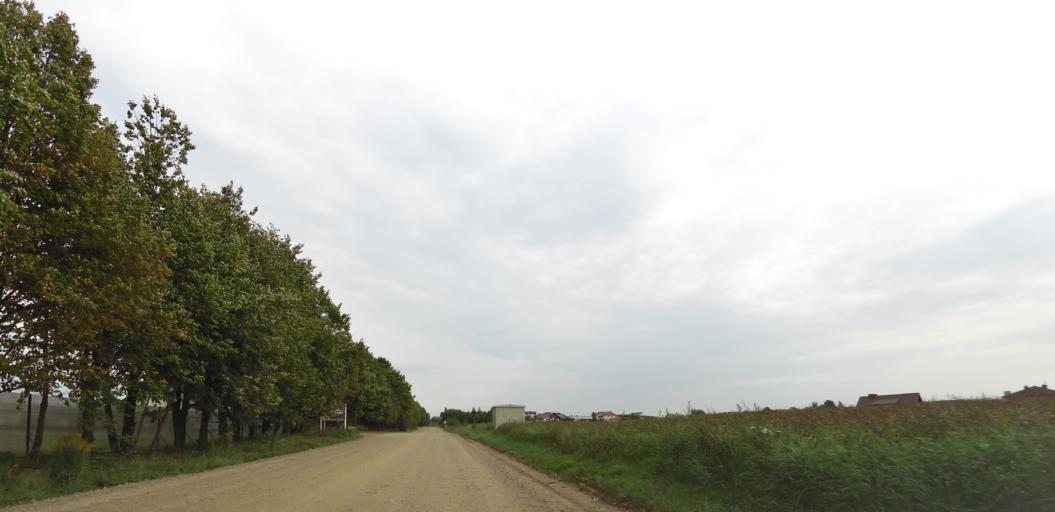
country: LT
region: Vilnius County
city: Pasilaiciai
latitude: 54.7598
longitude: 25.2220
